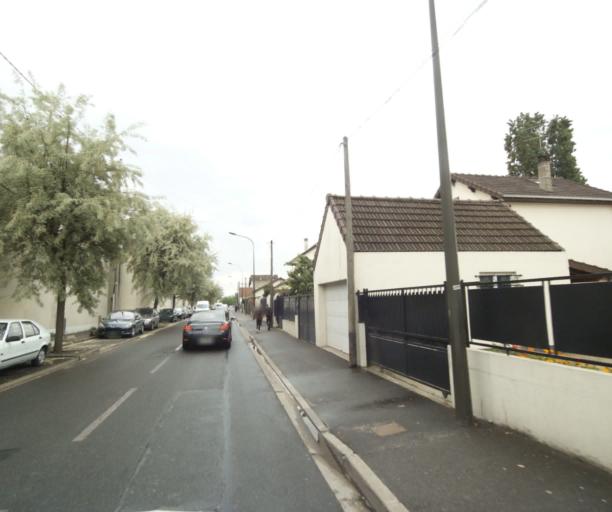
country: FR
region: Ile-de-France
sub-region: Departement du Val-d'Oise
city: Bezons
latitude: 48.9325
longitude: 2.2266
